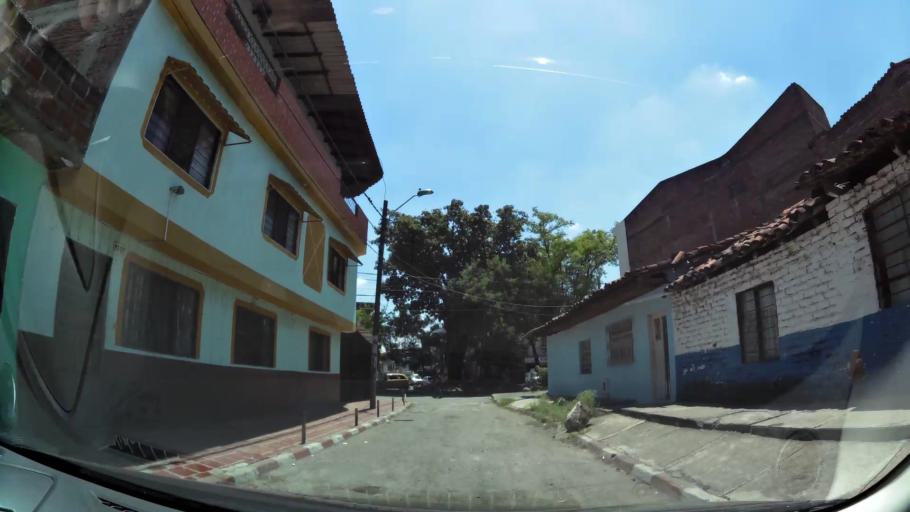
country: CO
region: Valle del Cauca
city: Cali
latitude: 3.4360
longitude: -76.5007
